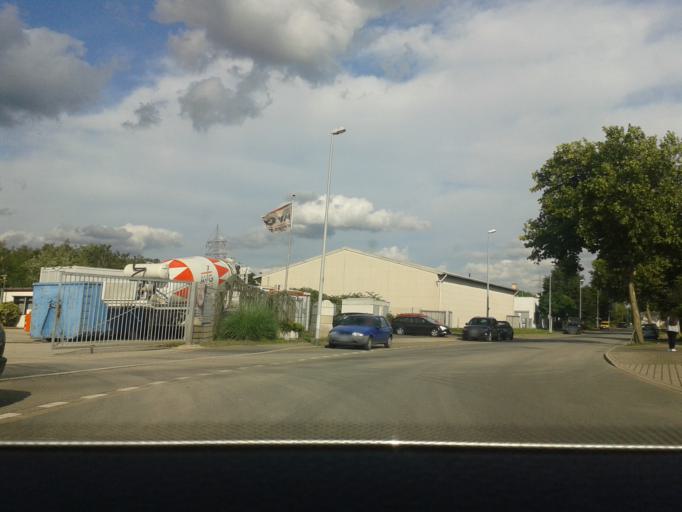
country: DE
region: North Rhine-Westphalia
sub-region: Regierungsbezirk Dusseldorf
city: Moers
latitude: 51.4217
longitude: 6.6871
